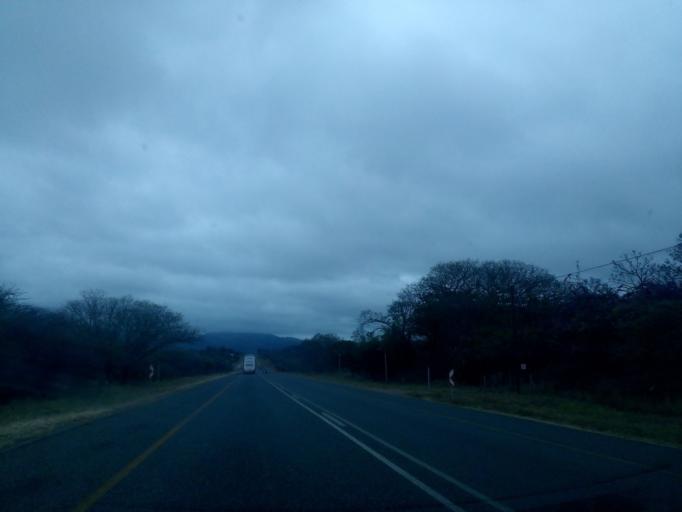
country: ZA
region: Limpopo
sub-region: Vhembe District Municipality
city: Louis Trichardt
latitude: -23.0875
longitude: 29.9056
